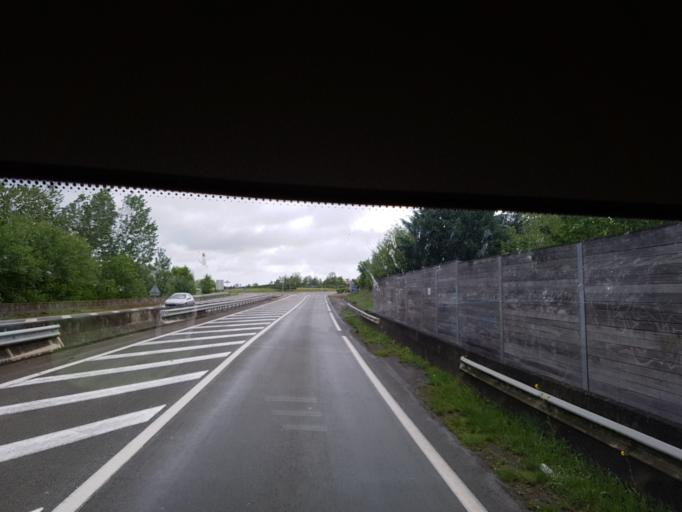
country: FR
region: Picardie
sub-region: Departement de l'Aisne
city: Courmelles
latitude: 49.3590
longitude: 3.3133
